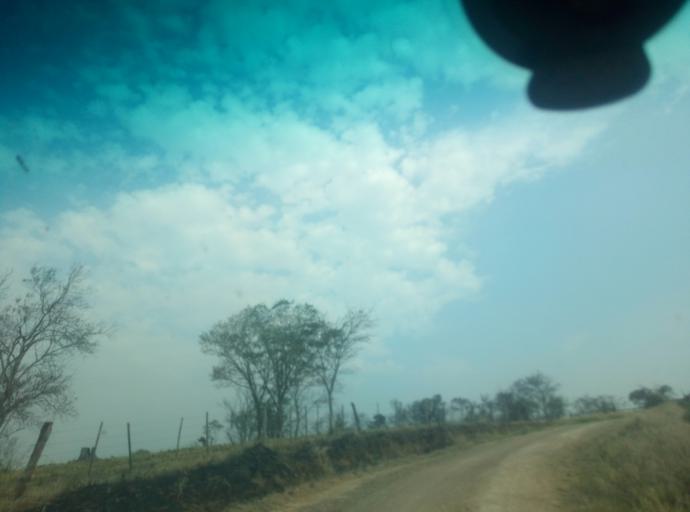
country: PY
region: Caaguazu
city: San Joaquin
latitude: -25.0900
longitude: -56.1405
